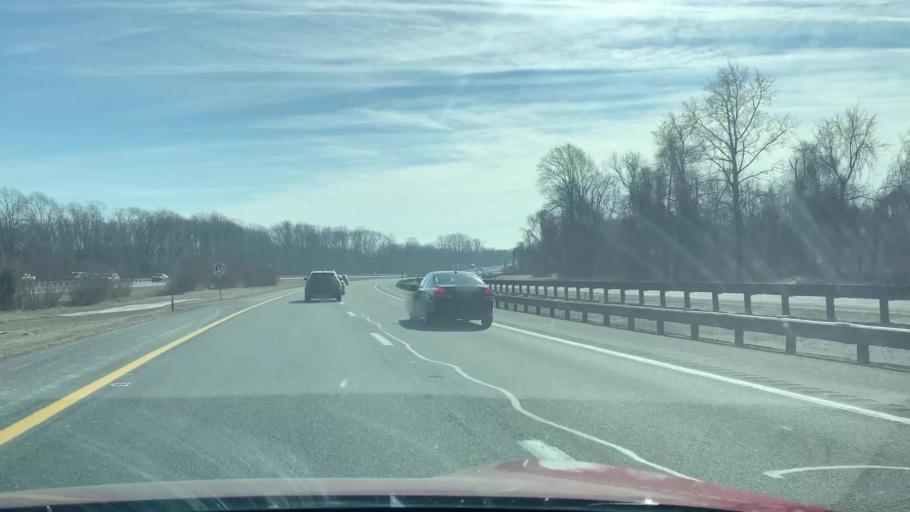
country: US
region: New Jersey
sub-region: Monmouth County
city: Lincroft
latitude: 40.3532
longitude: -74.1212
